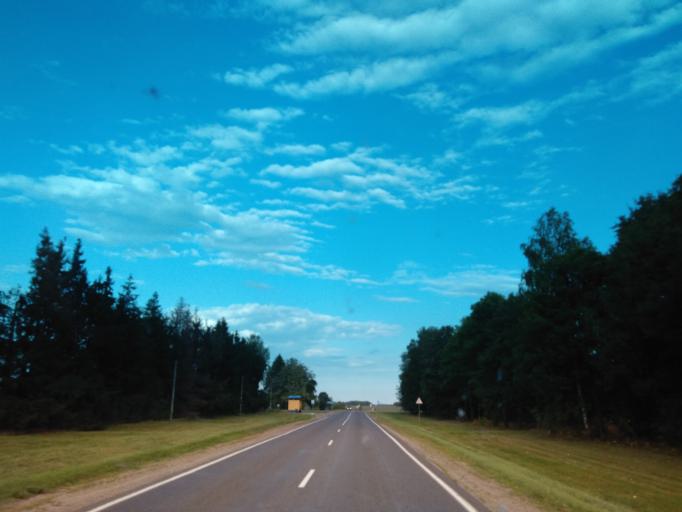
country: BY
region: Minsk
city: Uzda
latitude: 53.4378
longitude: 27.3254
